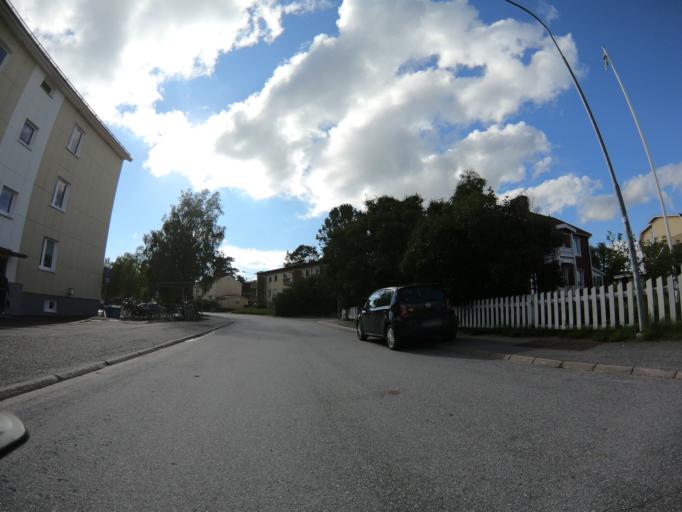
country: SE
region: Vaesterbotten
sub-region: Umea Kommun
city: Umea
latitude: 63.8364
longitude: 20.2803
